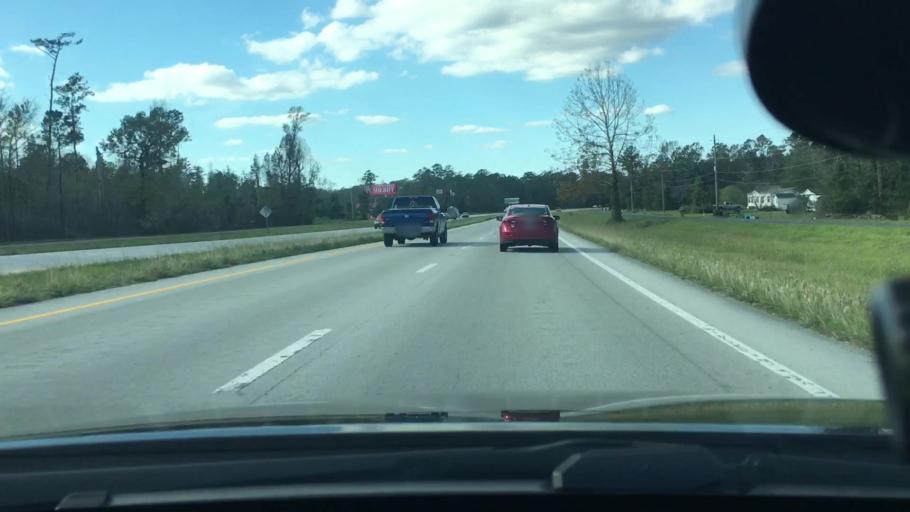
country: US
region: North Carolina
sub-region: Craven County
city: Neuse Forest
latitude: 34.9696
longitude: -76.9695
